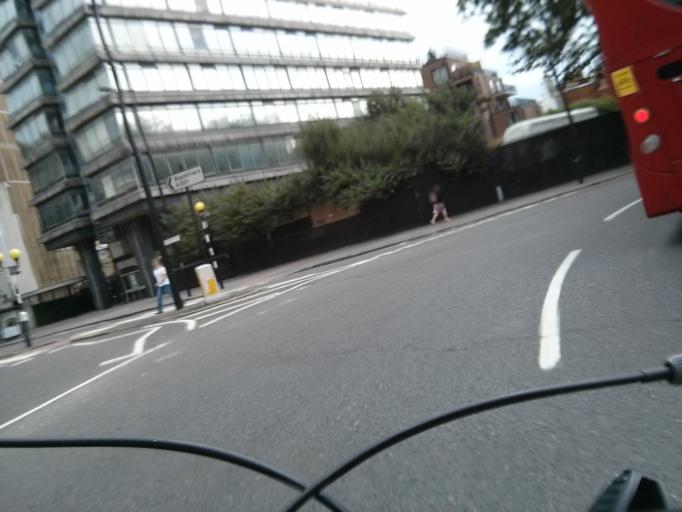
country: GB
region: England
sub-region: Greater London
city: Lambeth
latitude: 51.4989
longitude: -0.1049
